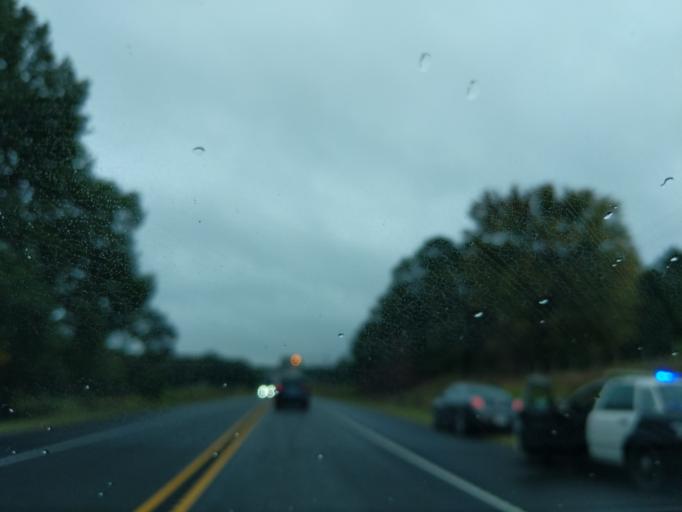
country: US
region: Louisiana
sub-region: Caddo Parish
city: Greenwood
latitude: 32.4379
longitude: -93.9831
